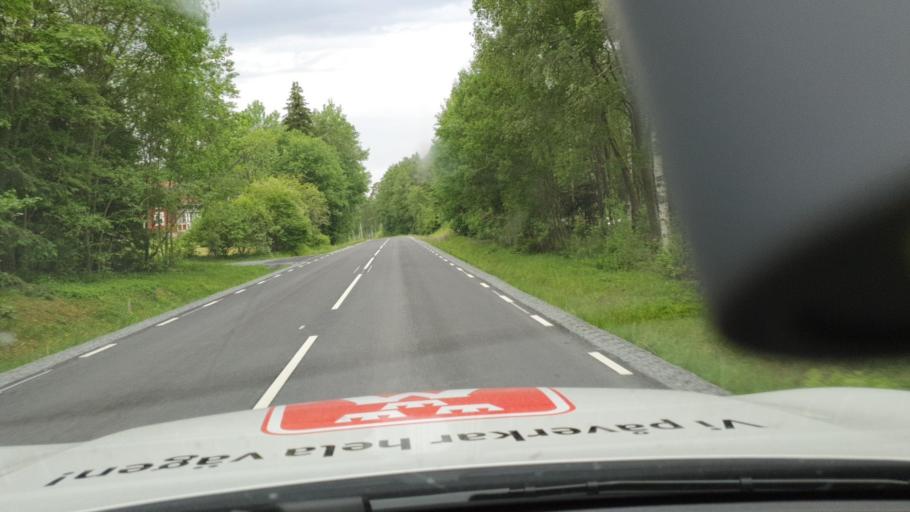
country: SE
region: Vaestra Goetaland
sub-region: Gullspangs Kommun
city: Anderstorp
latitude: 58.9176
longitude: 14.4448
